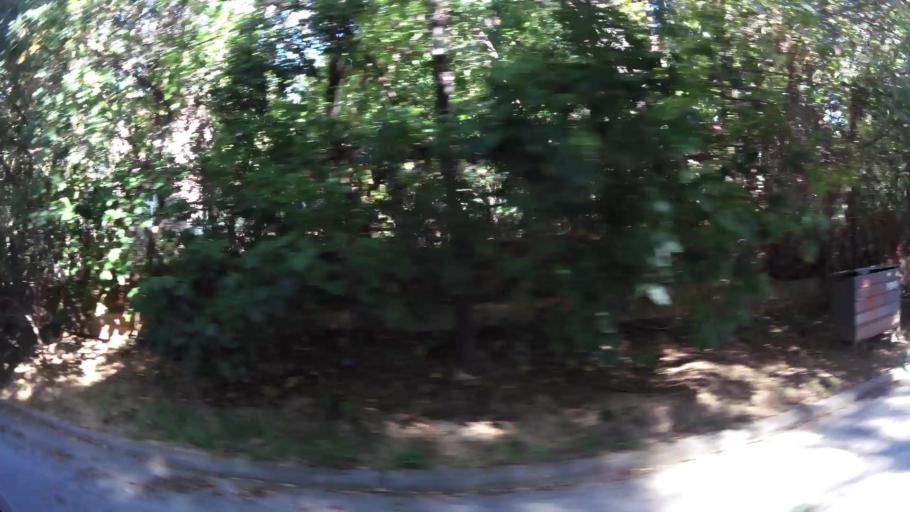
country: GR
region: Attica
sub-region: Nomarchia Athinas
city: Ekali
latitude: 38.1119
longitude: 23.8325
